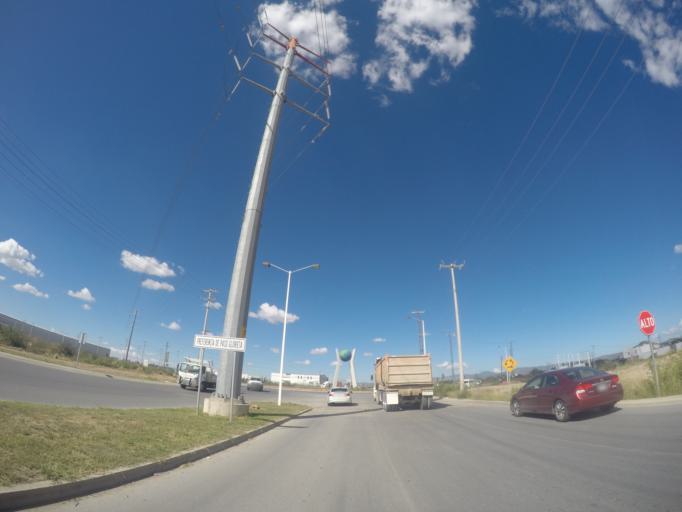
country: MX
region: San Luis Potosi
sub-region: Zaragoza
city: Cerro Gordo
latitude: 21.9831
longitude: -100.8555
